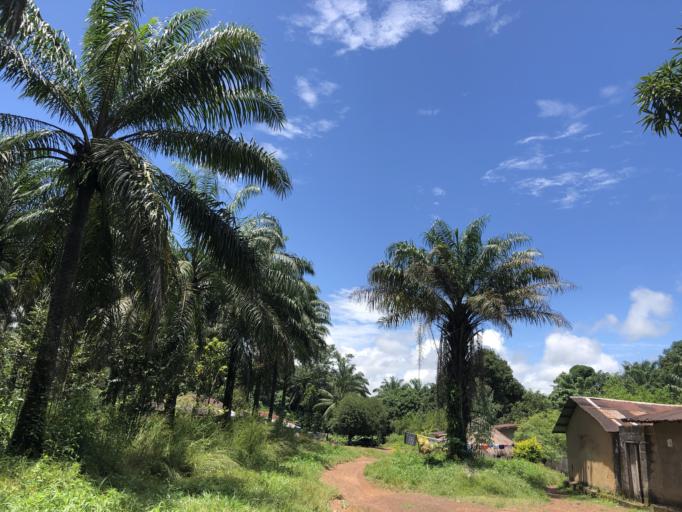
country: SL
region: Northern Province
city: Makeni
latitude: 8.8649
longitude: -12.1291
